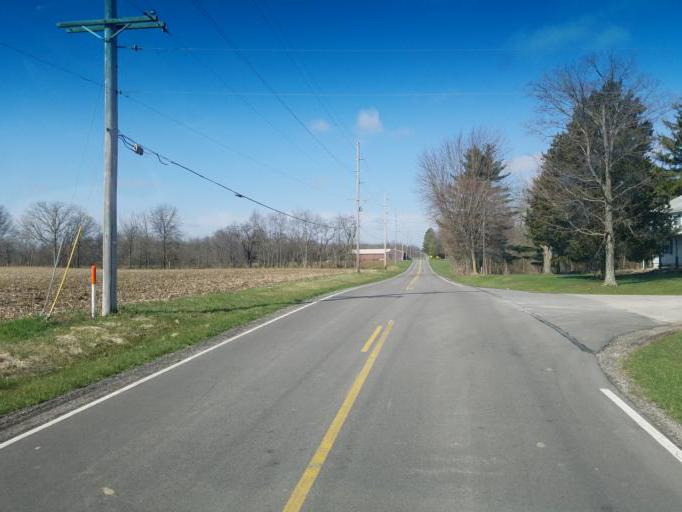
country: US
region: Ohio
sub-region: Crawford County
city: Bucyrus
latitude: 40.8336
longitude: -82.8717
